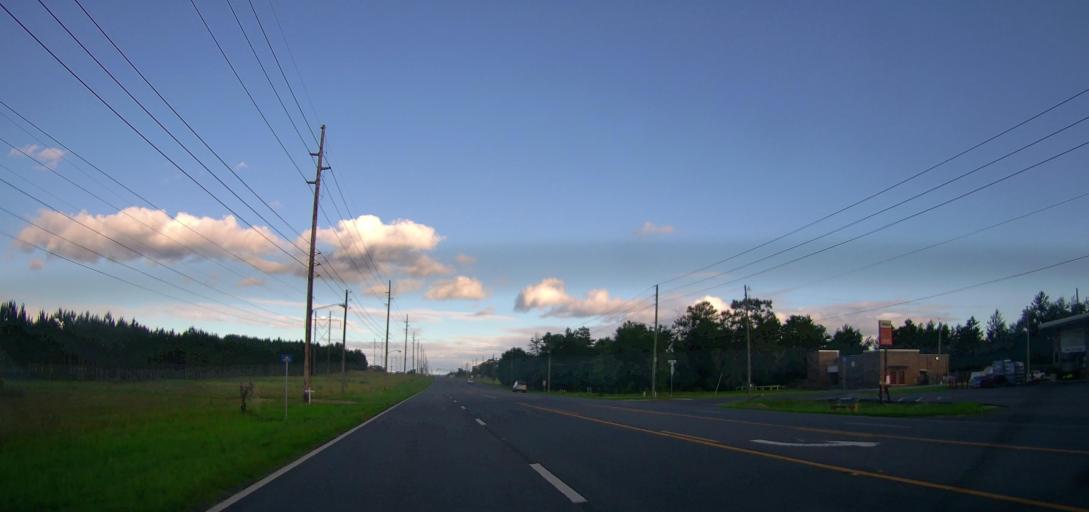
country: US
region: Florida
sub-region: Marion County
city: Silver Springs Shores
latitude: 29.0933
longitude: -82.0010
